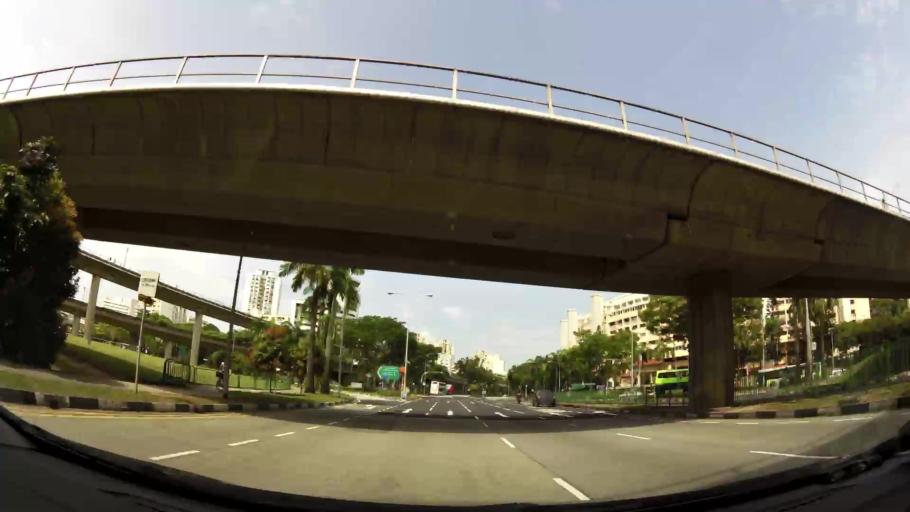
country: SG
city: Singapore
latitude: 1.3370
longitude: 103.7409
